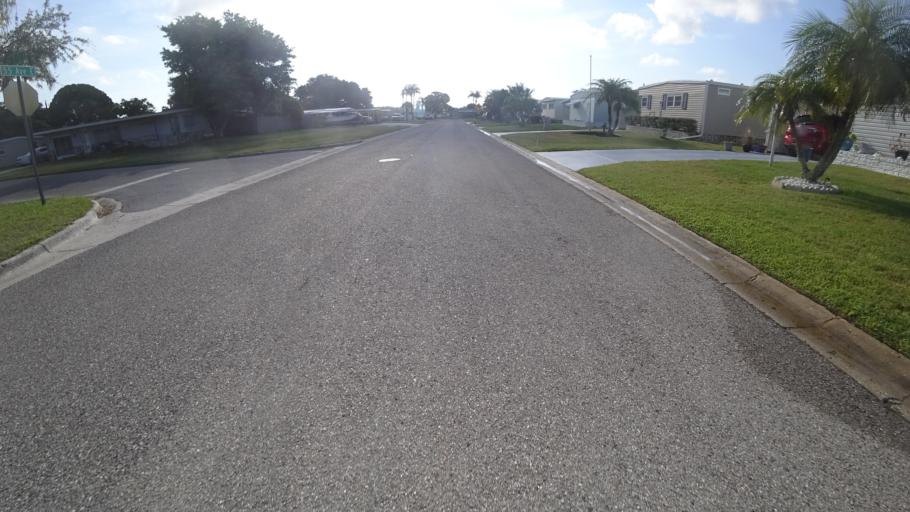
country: US
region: Florida
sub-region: Manatee County
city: West Samoset
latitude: 27.4439
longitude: -82.5596
